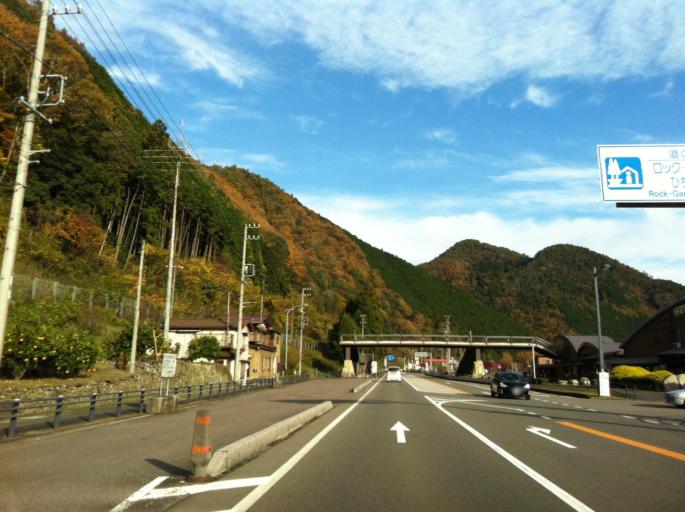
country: JP
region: Gifu
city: Minokamo
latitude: 35.5333
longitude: 137.1142
